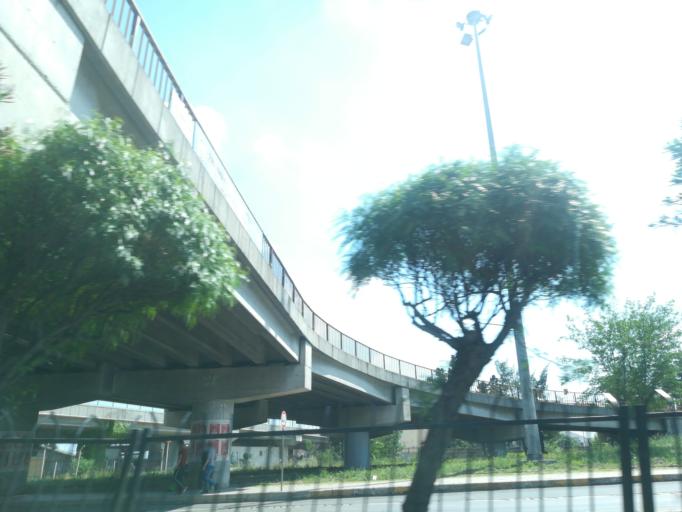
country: TR
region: Adana
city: Adana
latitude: 36.9890
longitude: 35.3435
